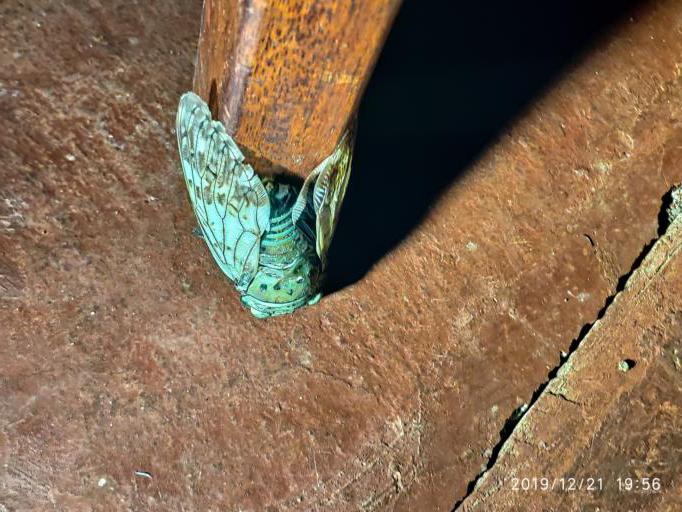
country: MG
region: Diana
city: Ambilobe
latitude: -12.9617
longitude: 49.1489
